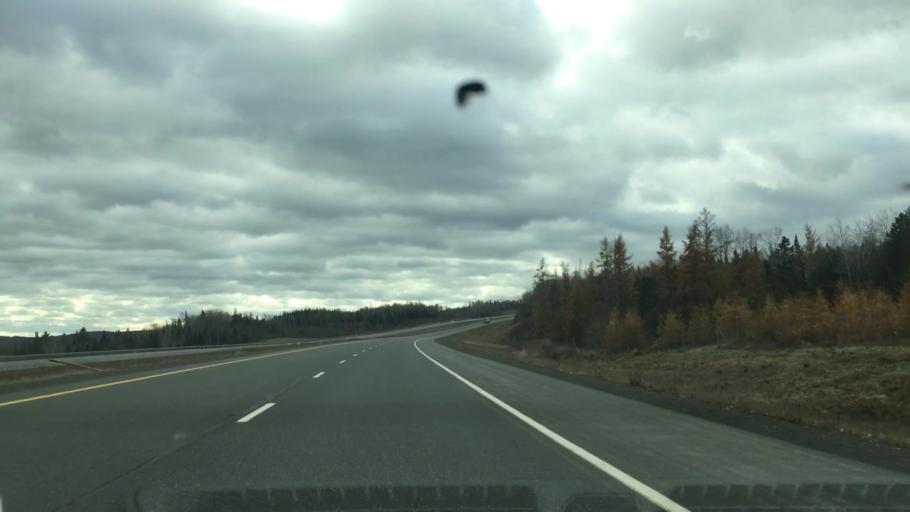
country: US
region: Maine
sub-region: Aroostook County
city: Fort Fairfield
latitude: 46.6705
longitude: -67.7301
